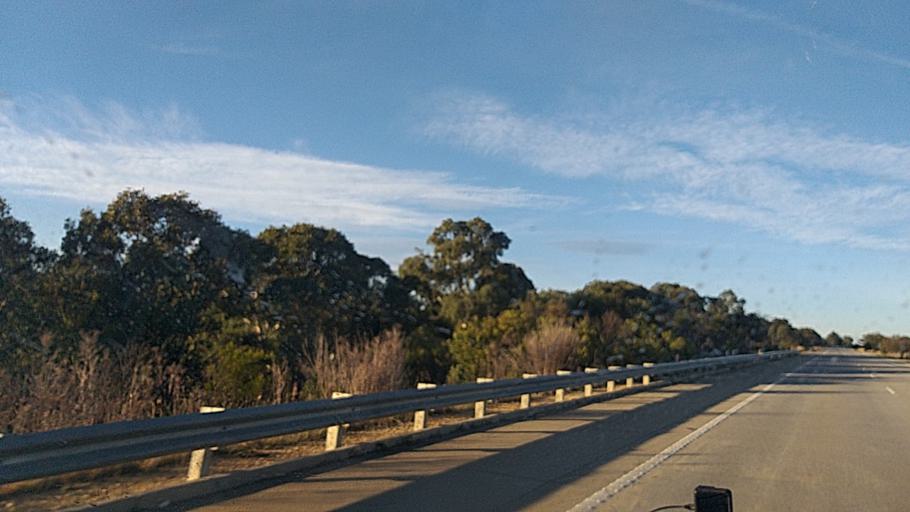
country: AU
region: New South Wales
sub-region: Yass Valley
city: Gundaroo
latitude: -35.1280
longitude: 149.3424
